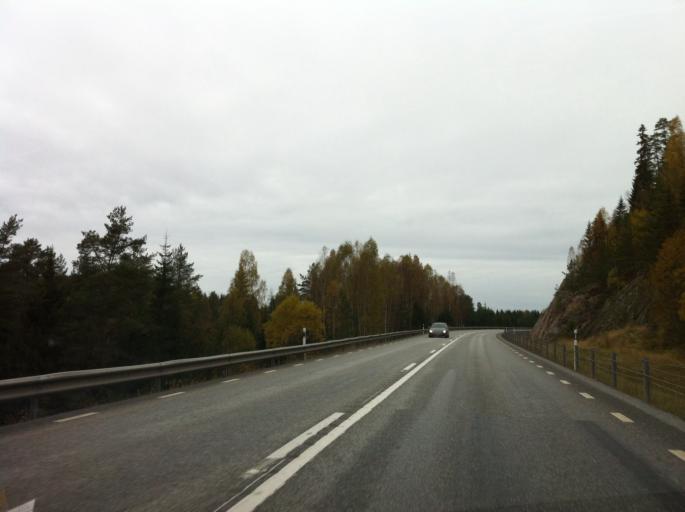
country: SE
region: OErebro
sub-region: Ljusnarsbergs Kommun
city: Kopparberg
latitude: 59.8509
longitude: 15.0638
